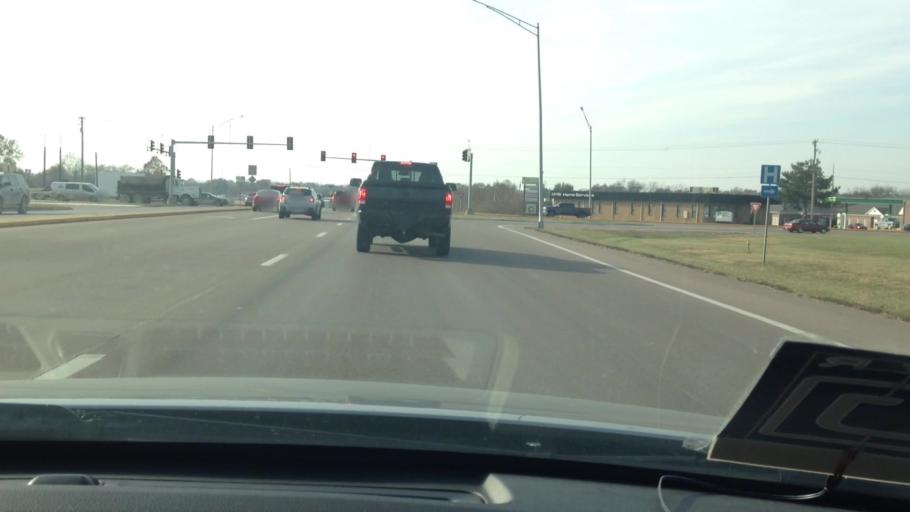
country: US
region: Missouri
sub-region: Henry County
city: Clinton
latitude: 38.3883
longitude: -93.7699
